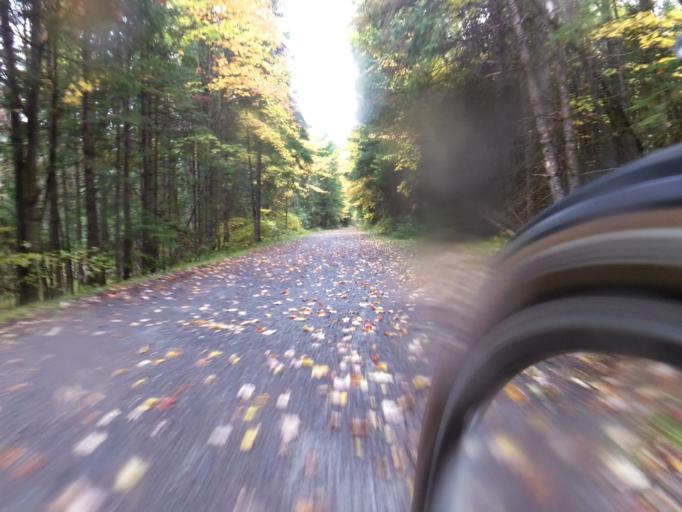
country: CA
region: Quebec
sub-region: Outaouais
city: Shawville
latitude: 45.6686
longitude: -76.5397
